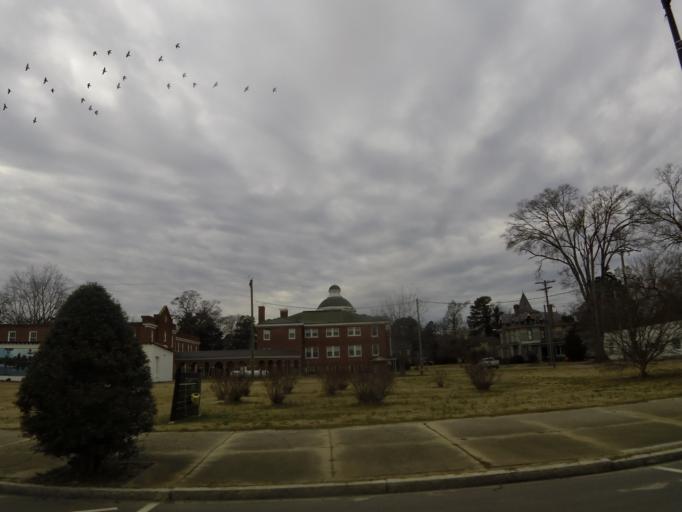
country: US
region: North Carolina
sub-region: Halifax County
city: Scotland Neck
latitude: 36.1306
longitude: -77.4236
